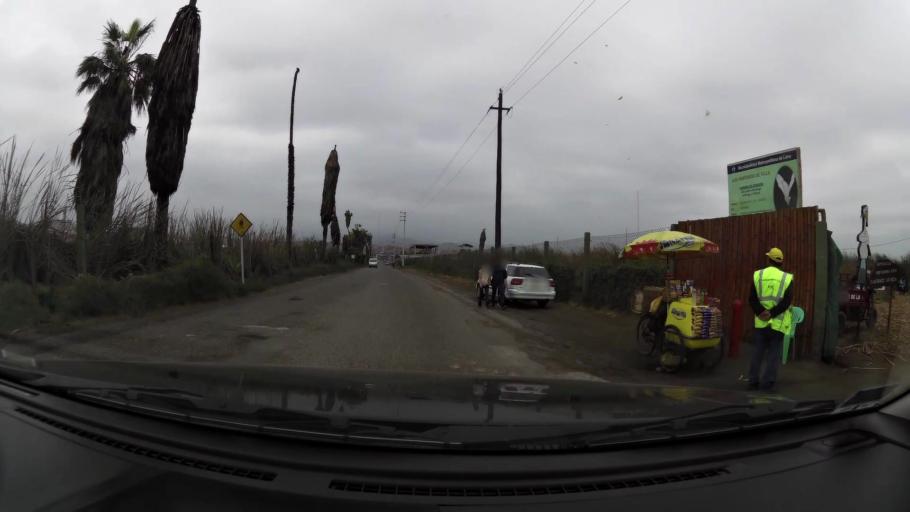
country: PE
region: Lima
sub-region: Lima
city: Surco
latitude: -12.2119
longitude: -76.9903
